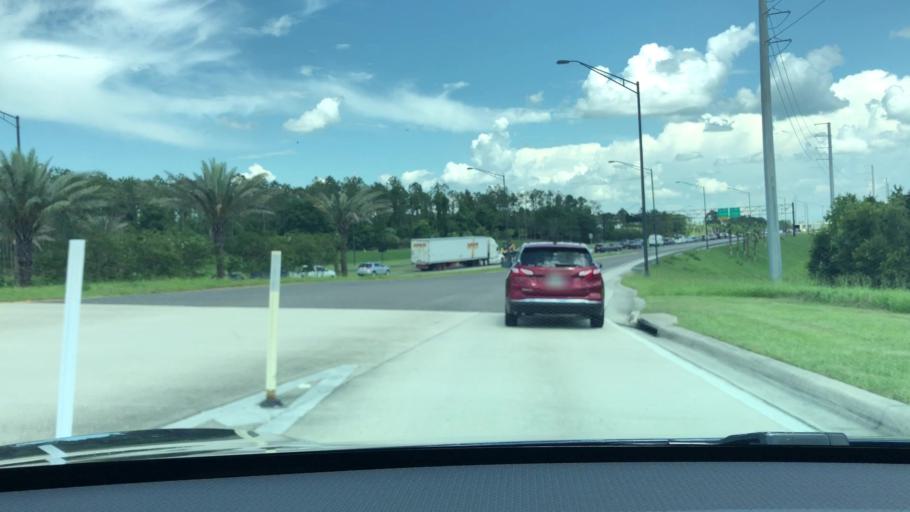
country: US
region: Florida
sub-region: Polk County
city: Citrus Ridge
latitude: 28.2933
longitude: -81.6021
